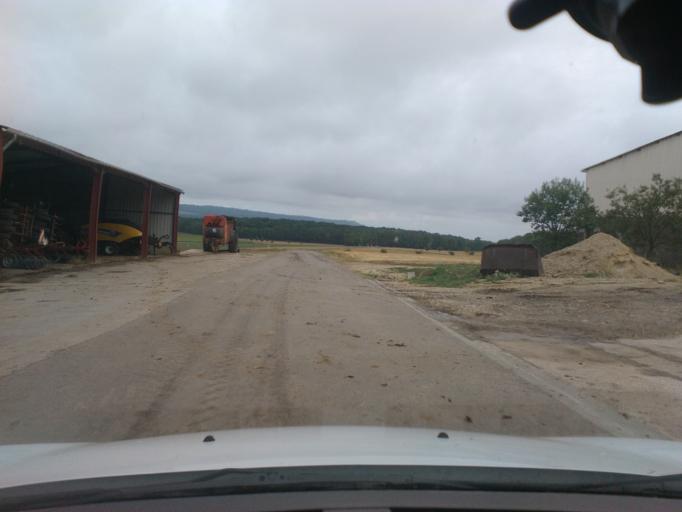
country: FR
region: Lorraine
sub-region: Departement des Vosges
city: Mirecourt
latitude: 48.3632
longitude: 6.1260
